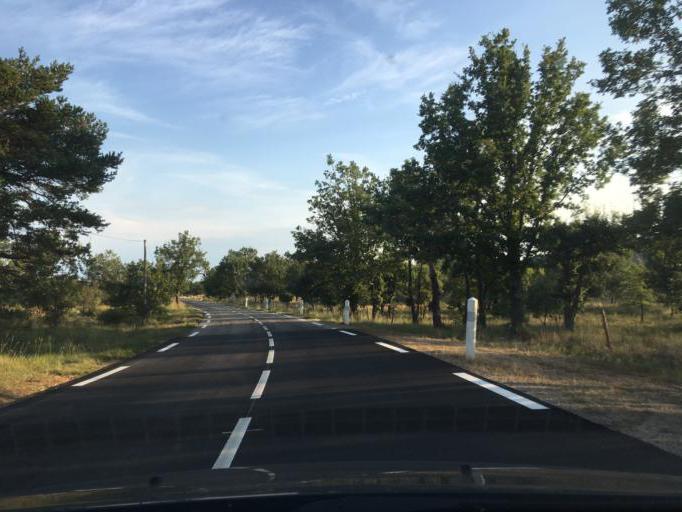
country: FR
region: Provence-Alpes-Cote d'Azur
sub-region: Departement du Var
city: Aups
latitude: 43.6857
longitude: 6.2235
